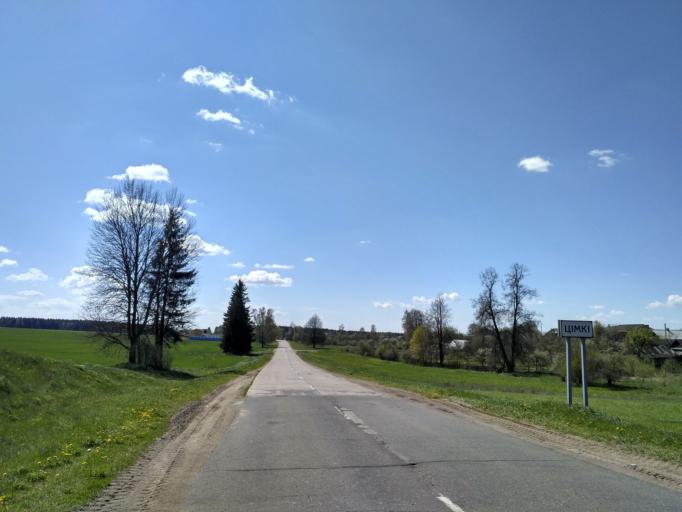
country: BY
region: Minsk
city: Horad Barysaw
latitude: 54.3660
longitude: 28.4697
